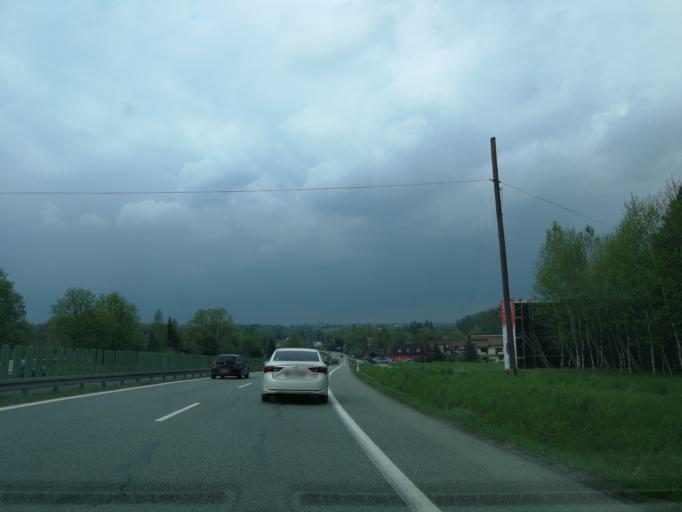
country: PL
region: Lesser Poland Voivodeship
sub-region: Powiat myslenicki
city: Jawornik
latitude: 49.8672
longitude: 19.9092
